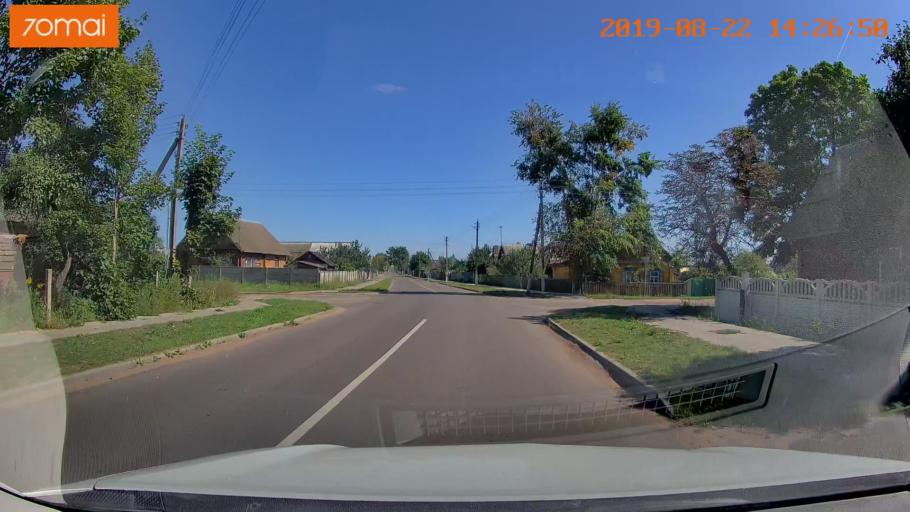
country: BY
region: Mogilev
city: Asipovichy
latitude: 53.2984
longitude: 28.6186
